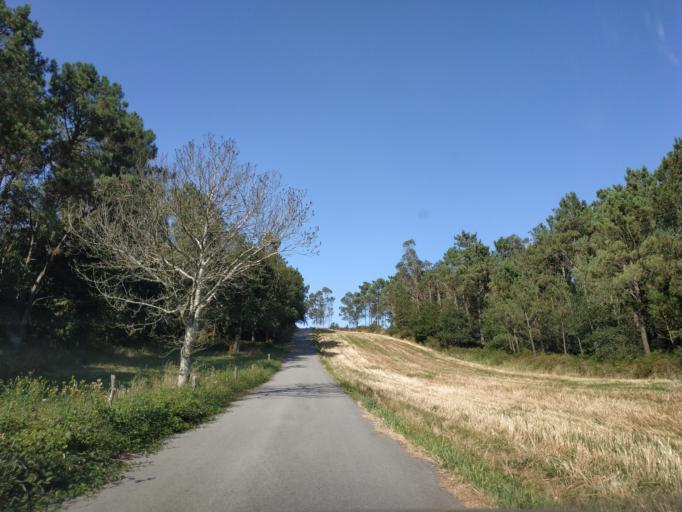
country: ES
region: Galicia
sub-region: Provincia da Coruna
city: Laracha
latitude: 43.2279
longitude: -8.5352
